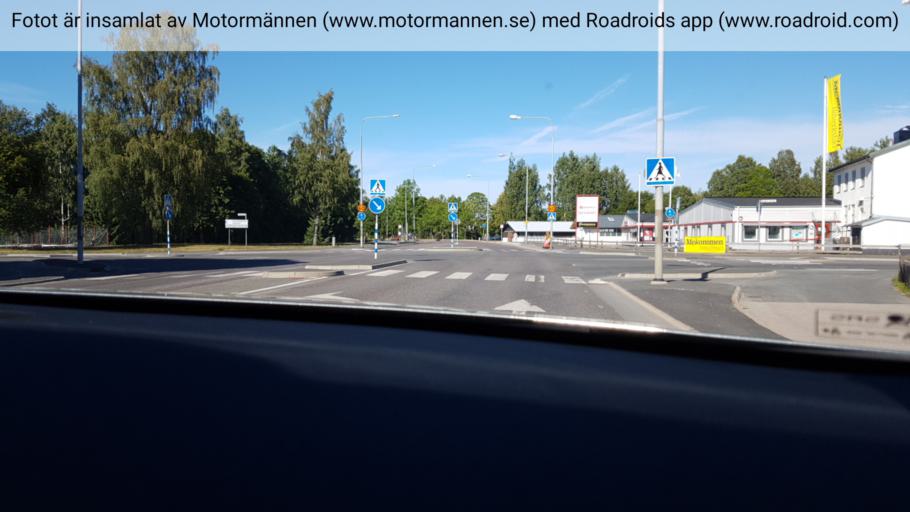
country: SE
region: Joenkoeping
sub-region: Varnamo Kommun
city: Varnamo
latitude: 57.1855
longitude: 14.0596
